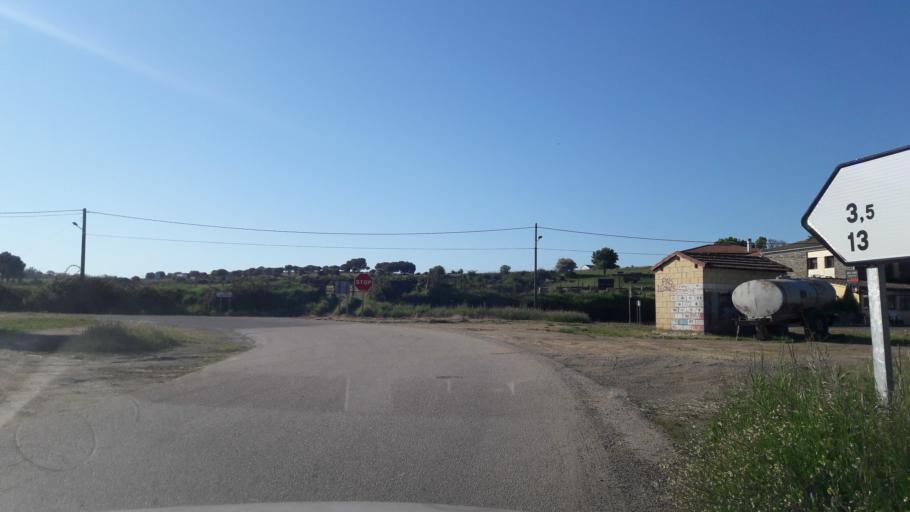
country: ES
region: Castille and Leon
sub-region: Provincia de Salamanca
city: Endrinal
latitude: 40.5934
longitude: -5.8024
